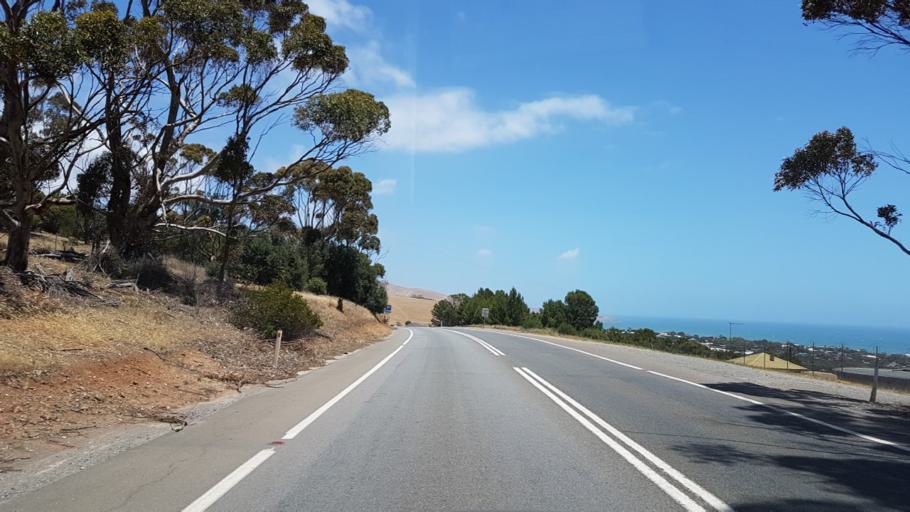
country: AU
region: South Australia
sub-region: Onkaparinga
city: Aldinga
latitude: -35.3386
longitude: 138.4642
